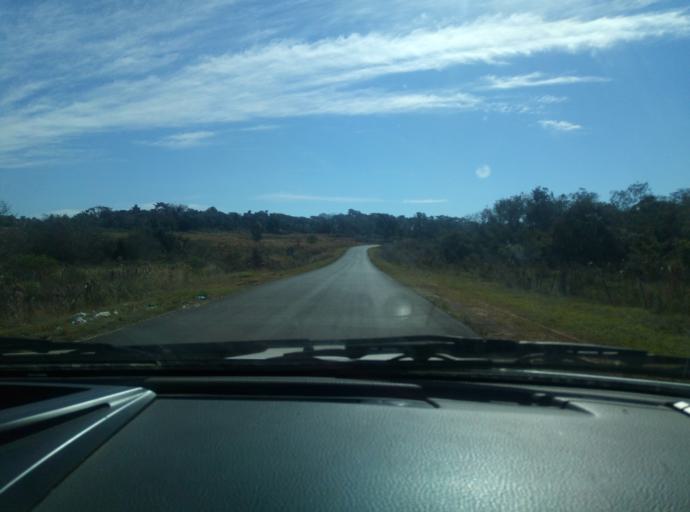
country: PY
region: Caaguazu
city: Carayao
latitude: -25.1797
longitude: -56.3126
